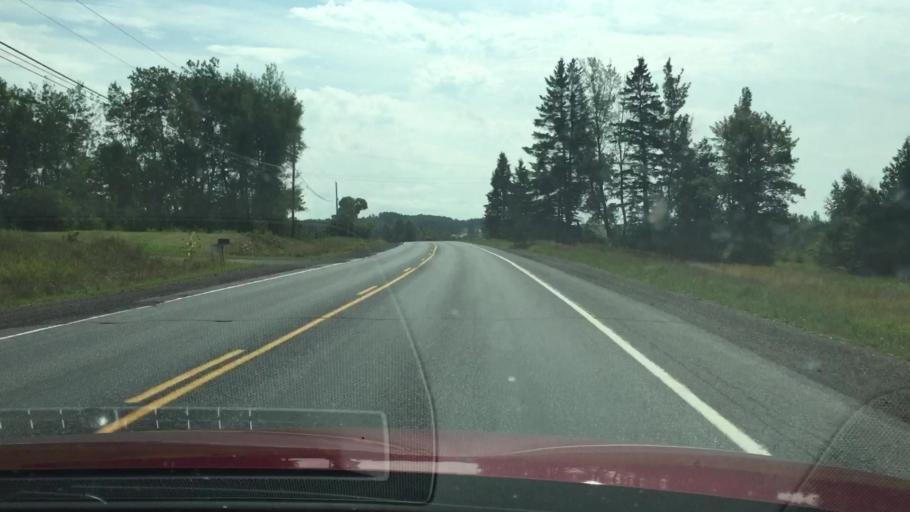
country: US
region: Maine
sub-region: Aroostook County
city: Easton
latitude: 46.6055
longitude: -67.9746
